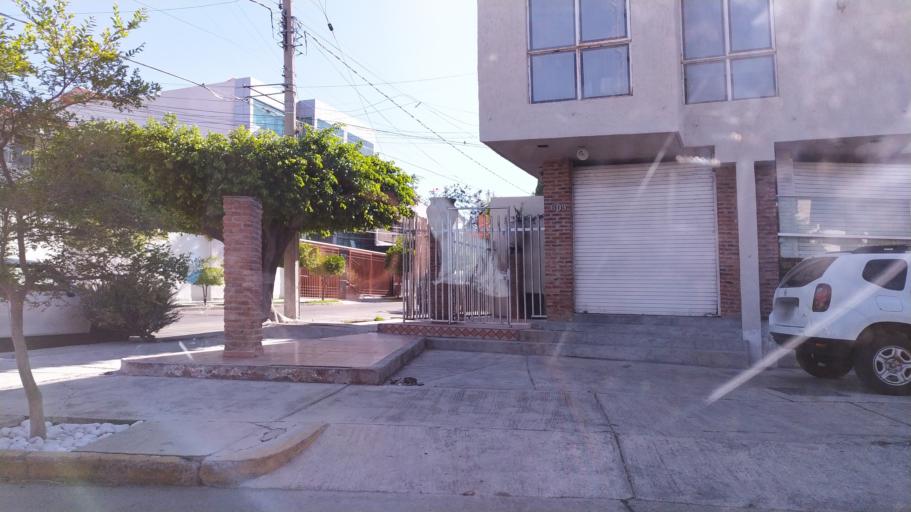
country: MX
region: Jalisco
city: Guadalajara
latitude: 20.6869
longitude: -103.3903
